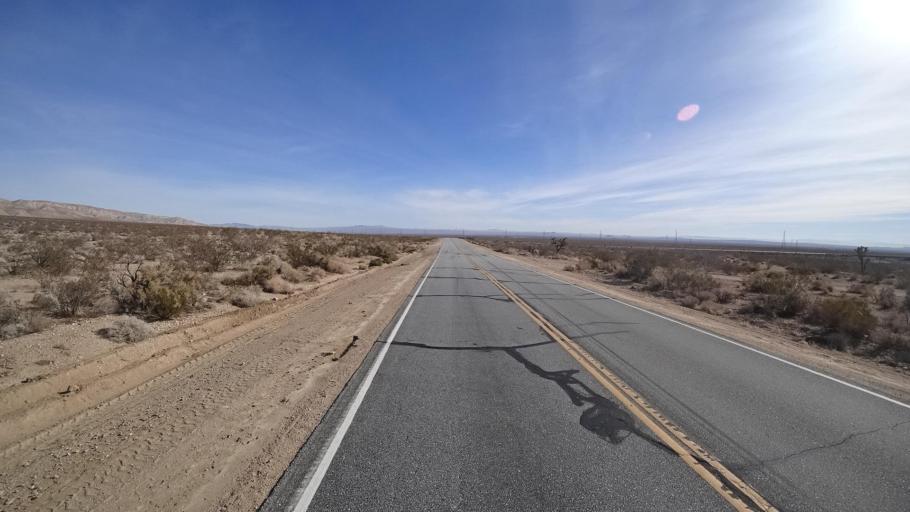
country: US
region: California
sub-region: Kern County
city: Mojave
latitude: 35.1241
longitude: -118.1796
